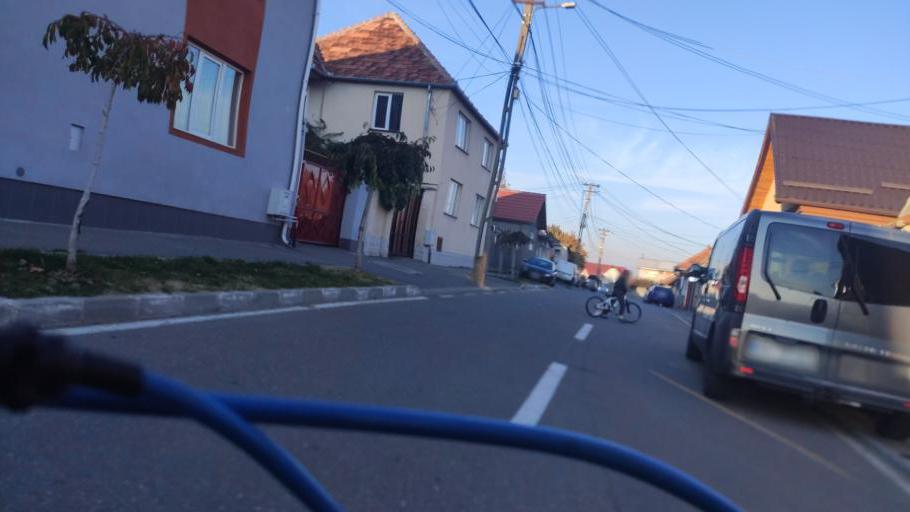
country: RO
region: Brasov
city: Codlea
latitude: 45.6932
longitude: 25.4411
